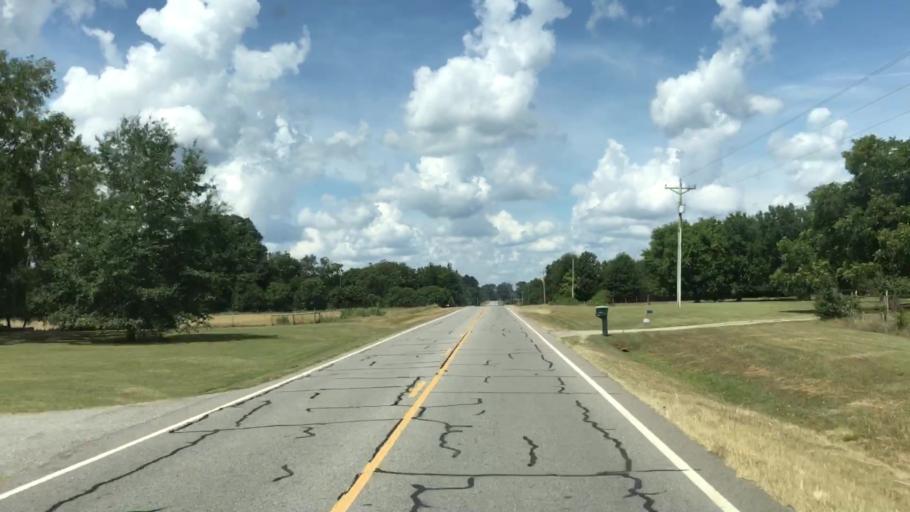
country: US
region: Georgia
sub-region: Oconee County
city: Watkinsville
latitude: 33.8289
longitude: -83.3753
